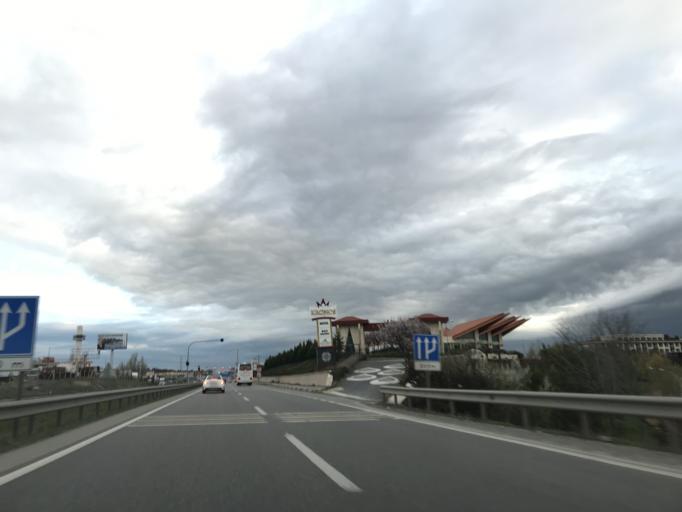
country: TR
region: Ankara
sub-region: Goelbasi
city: Golbasi
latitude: 39.7763
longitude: 32.8045
